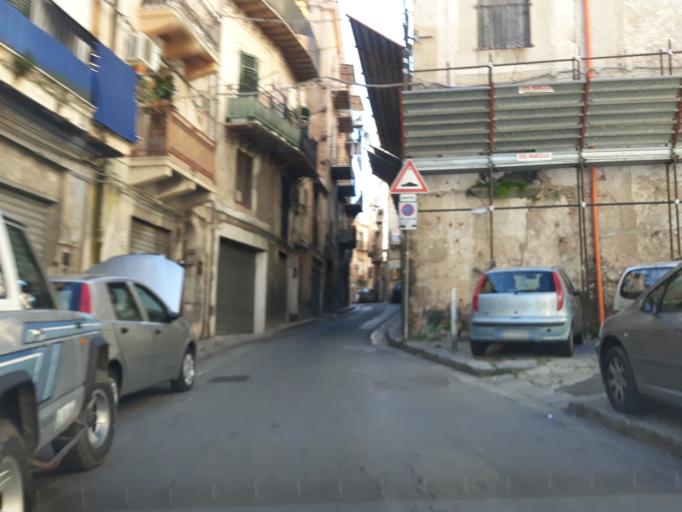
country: IT
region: Sicily
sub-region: Palermo
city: Monreale
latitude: 38.0836
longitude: 13.2927
